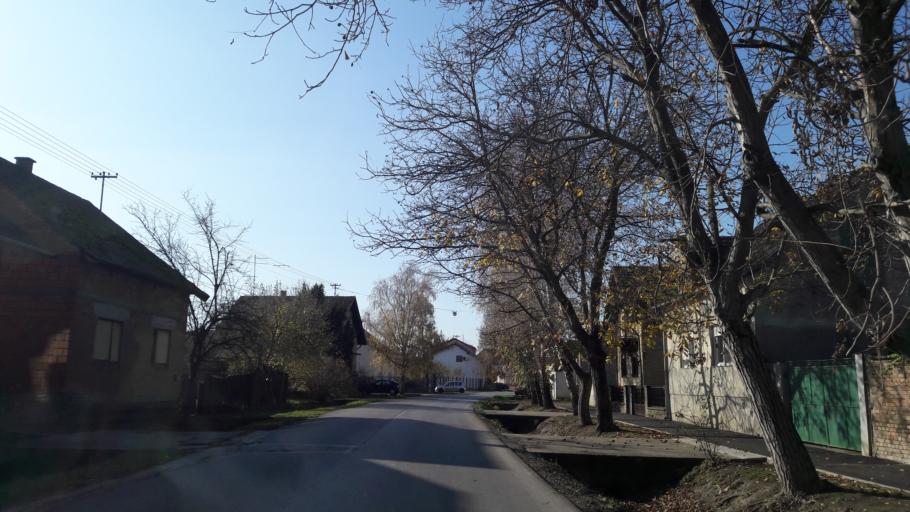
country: HR
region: Osjecko-Baranjska
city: Tenja
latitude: 45.4957
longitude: 18.7410
